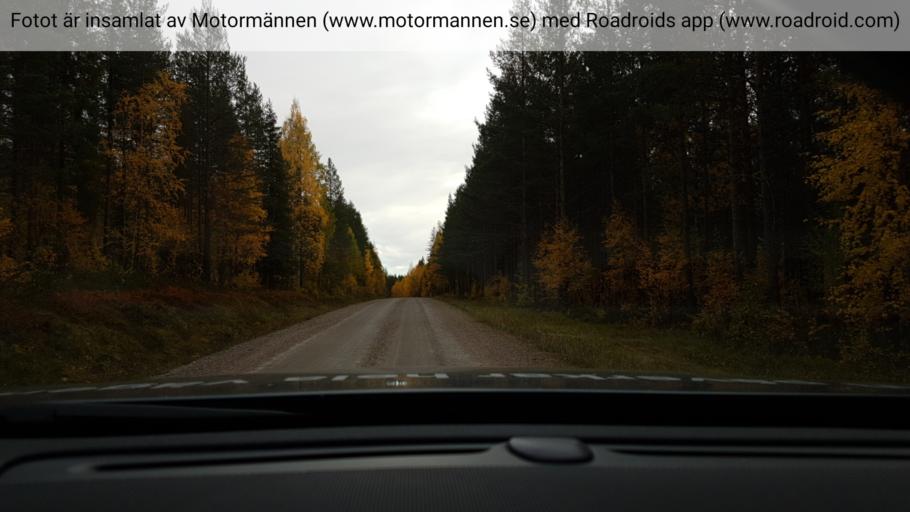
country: SE
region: Norrbotten
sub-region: Overkalix Kommun
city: OEverkalix
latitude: 66.2762
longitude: 22.9849
